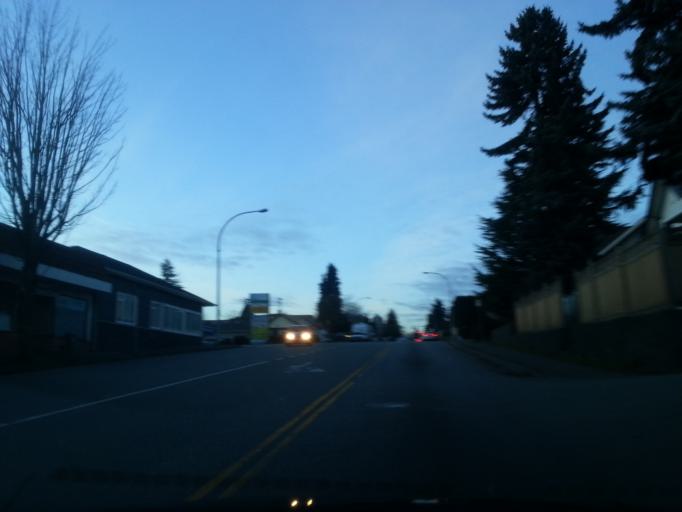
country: CA
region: British Columbia
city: New Westminster
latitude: 49.2031
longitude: -122.9486
